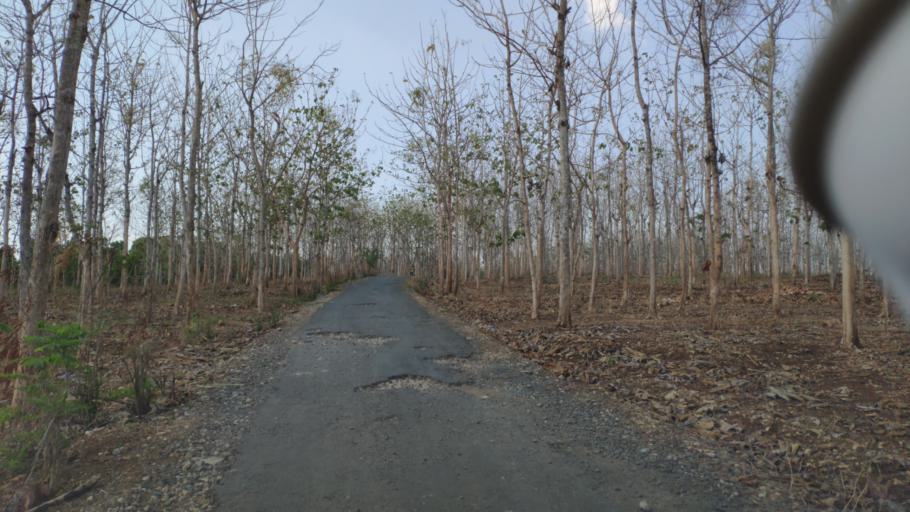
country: ID
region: Central Java
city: Ngapus
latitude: -6.9751
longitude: 111.1591
